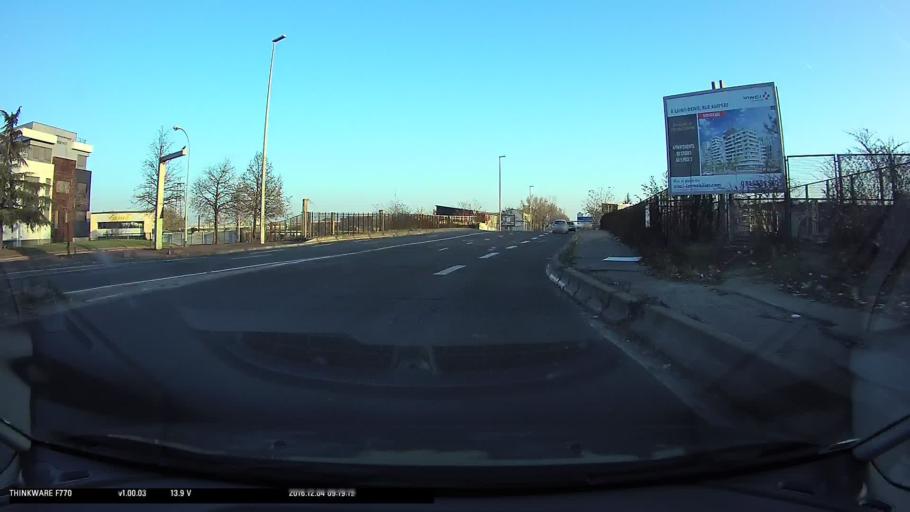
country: FR
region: Ile-de-France
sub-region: Departement de Seine-Saint-Denis
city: Saint-Denis
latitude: 48.9231
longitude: 2.3480
